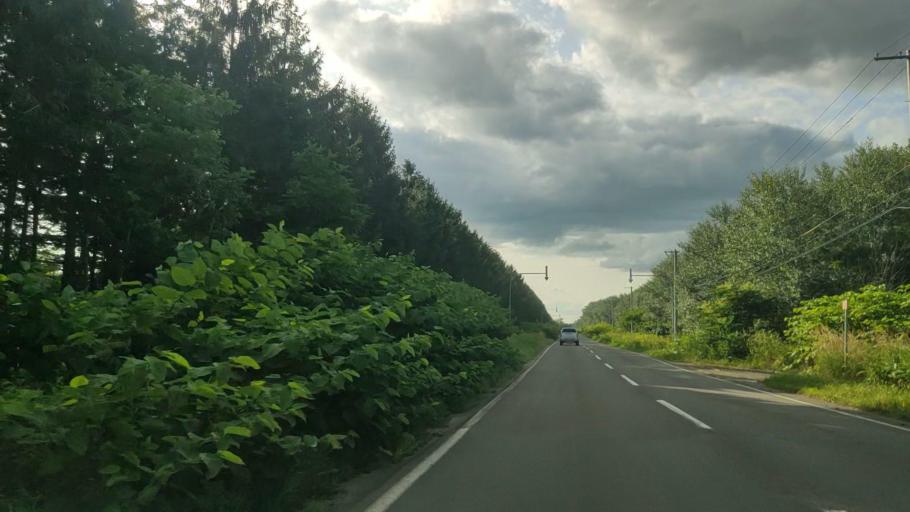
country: JP
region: Hokkaido
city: Makubetsu
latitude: 44.8988
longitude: 141.9145
